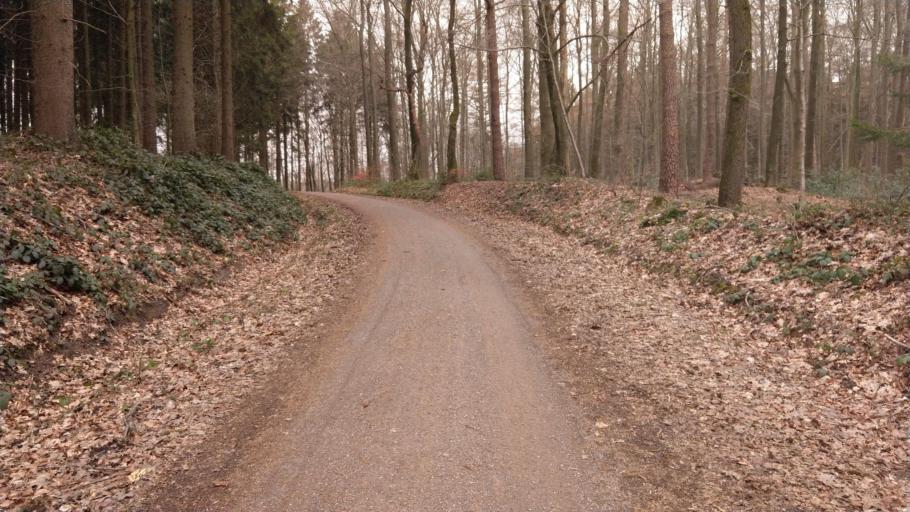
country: DE
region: North Rhine-Westphalia
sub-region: Regierungsbezirk Koln
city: Aachen
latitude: 50.7318
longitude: 6.0663
